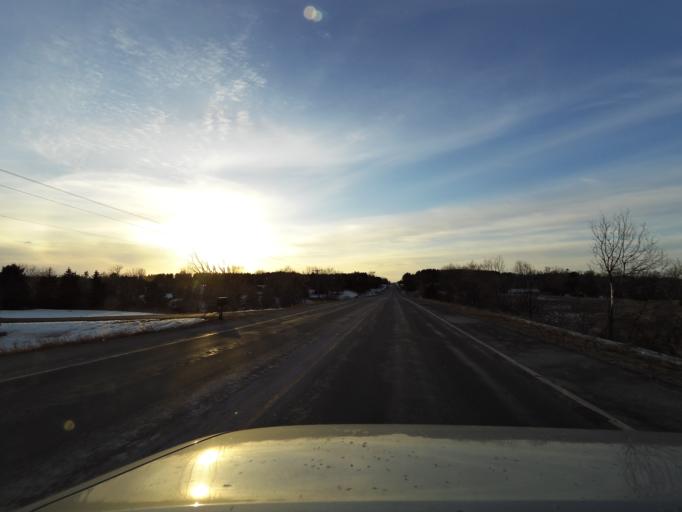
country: US
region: Wisconsin
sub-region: Saint Croix County
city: Hudson
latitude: 44.9780
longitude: -92.7062
